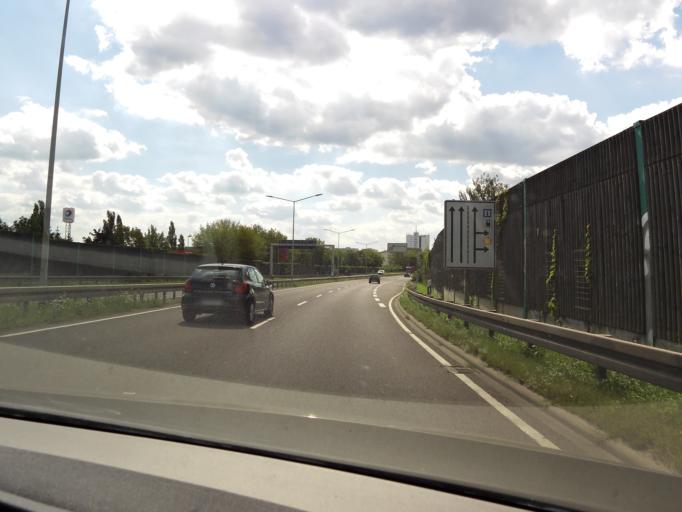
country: DE
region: Saxony-Anhalt
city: Barleben
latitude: 52.1796
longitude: 11.6274
